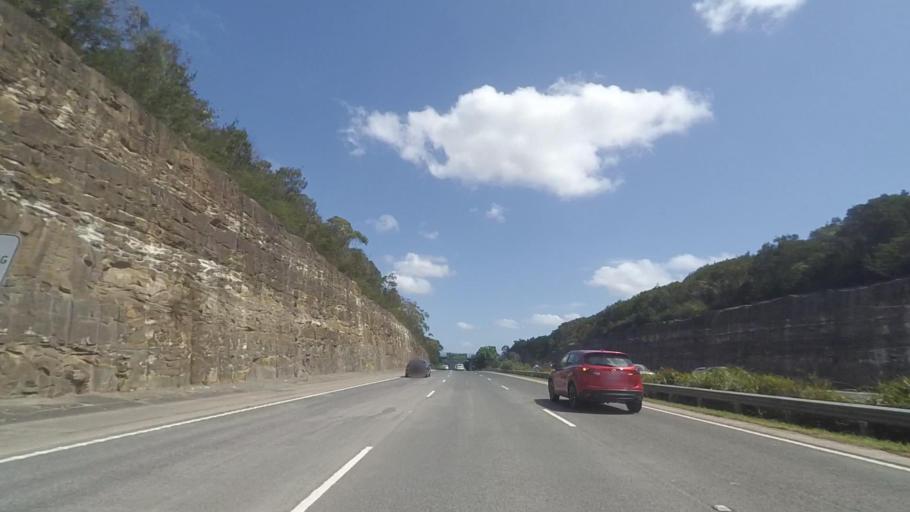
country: AU
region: New South Wales
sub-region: Hornsby Shire
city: Mount Colah
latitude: -33.6764
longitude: 151.1200
